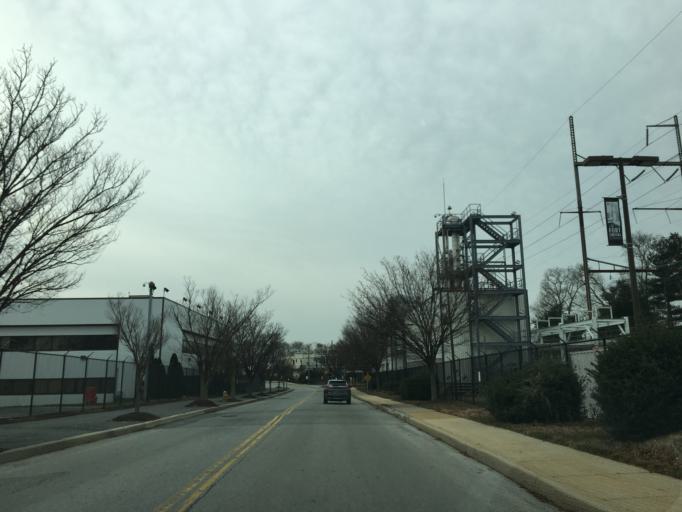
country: US
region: Delaware
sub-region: New Castle County
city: Wilmington
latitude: 39.7381
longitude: -75.5392
